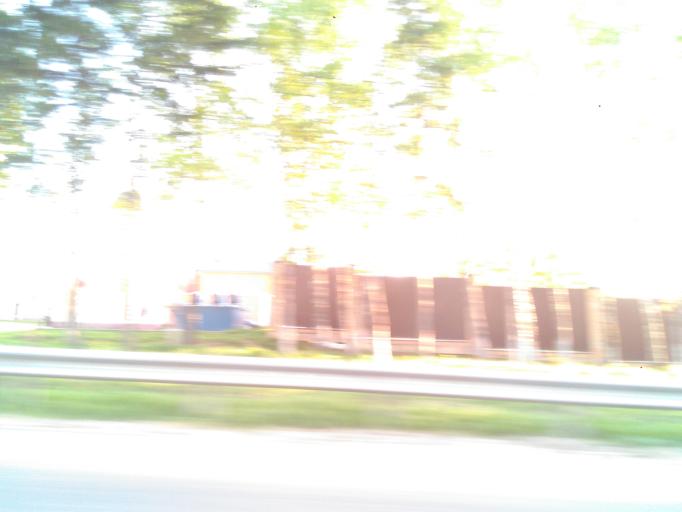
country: RU
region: Moskovskaya
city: Povarovo
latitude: 56.0268
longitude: 36.9880
